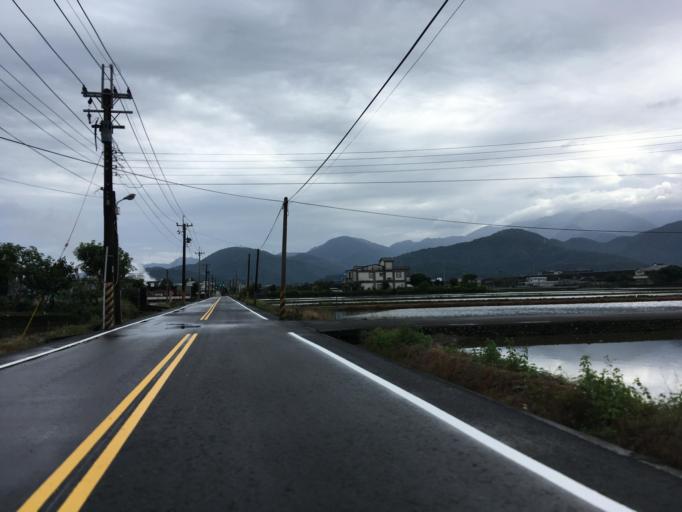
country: TW
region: Taiwan
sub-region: Yilan
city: Yilan
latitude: 24.6406
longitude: 121.8080
